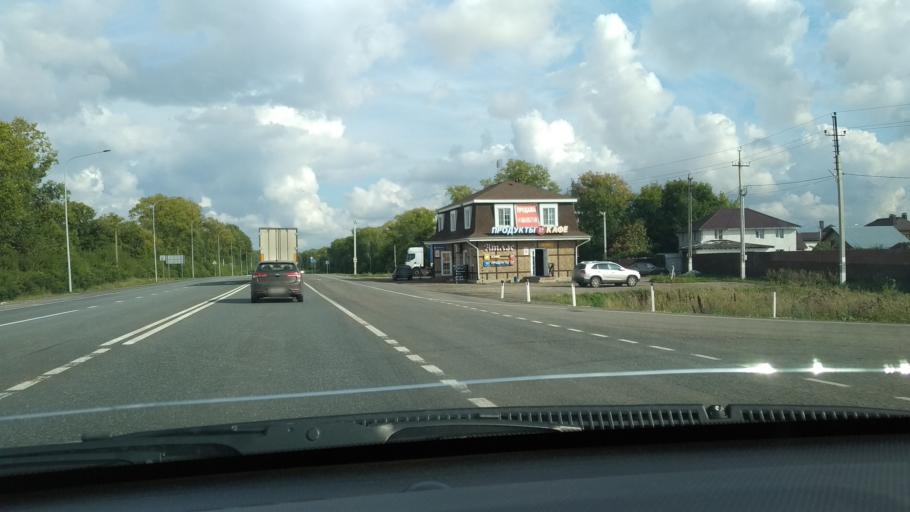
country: RU
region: Tatarstan
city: Stolbishchi
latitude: 55.6558
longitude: 49.3118
